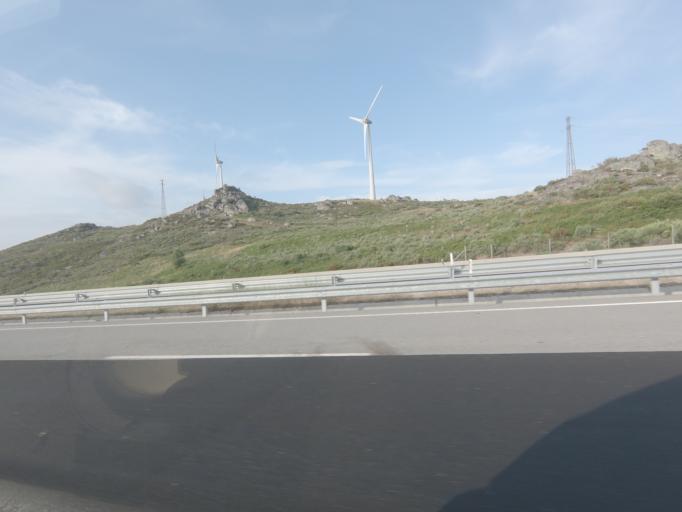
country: PT
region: Vila Real
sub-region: Vila Pouca de Aguiar
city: Vila Pouca de Aguiar
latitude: 41.4445
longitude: -7.6471
